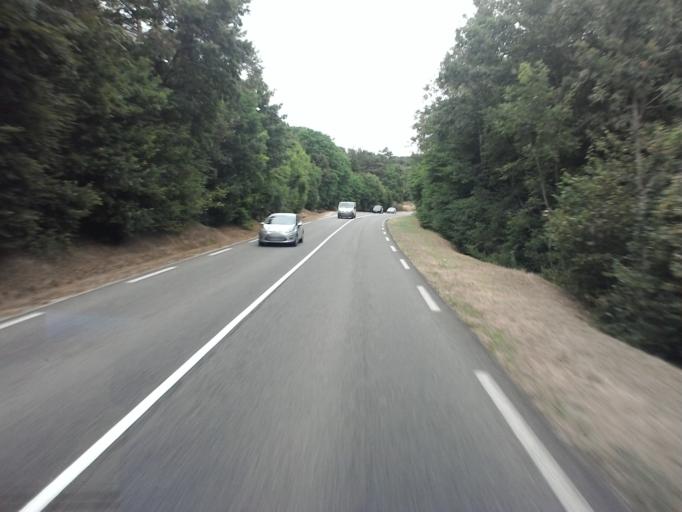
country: FR
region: Lorraine
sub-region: Departement de Meurthe-et-Moselle
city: Colombey-les-Belles
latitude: 48.5651
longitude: 5.9415
